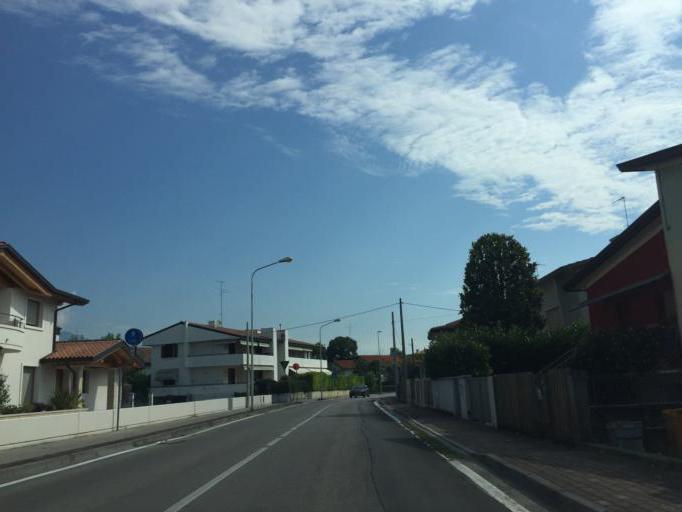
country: IT
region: Friuli Venezia Giulia
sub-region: Provincia di Pordenone
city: Sacile
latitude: 45.9560
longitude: 12.4917
